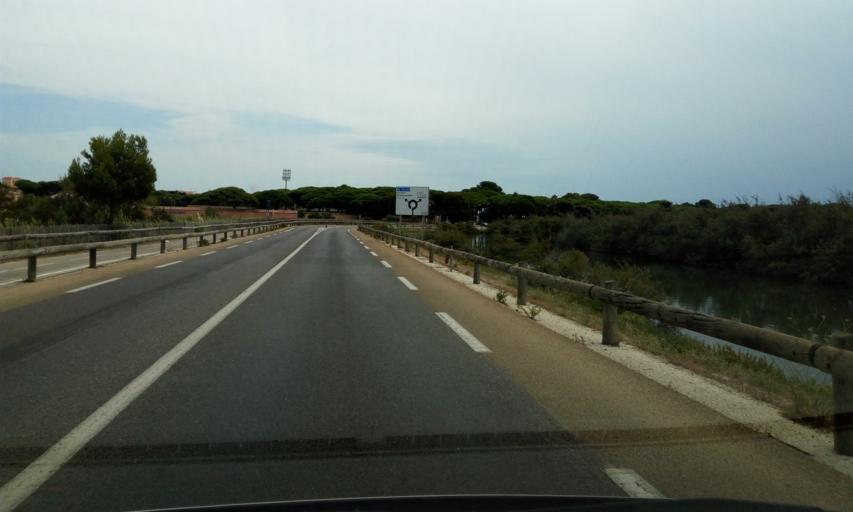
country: FR
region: Provence-Alpes-Cote d'Azur
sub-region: Departement du Var
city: Hyeres
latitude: 43.0815
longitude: 6.1470
